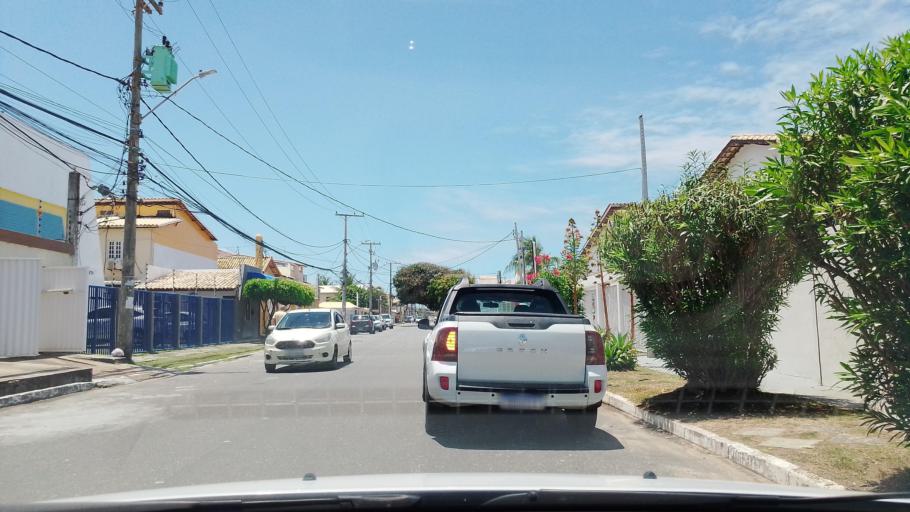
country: BR
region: Bahia
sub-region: Lauro De Freitas
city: Lauro de Freitas
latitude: -12.9393
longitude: -38.3326
